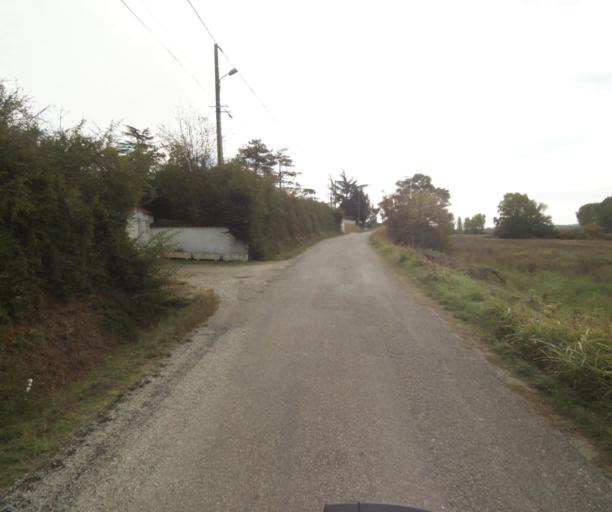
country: FR
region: Midi-Pyrenees
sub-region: Departement du Tarn-et-Garonne
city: Finhan
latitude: 43.9034
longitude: 1.2240
